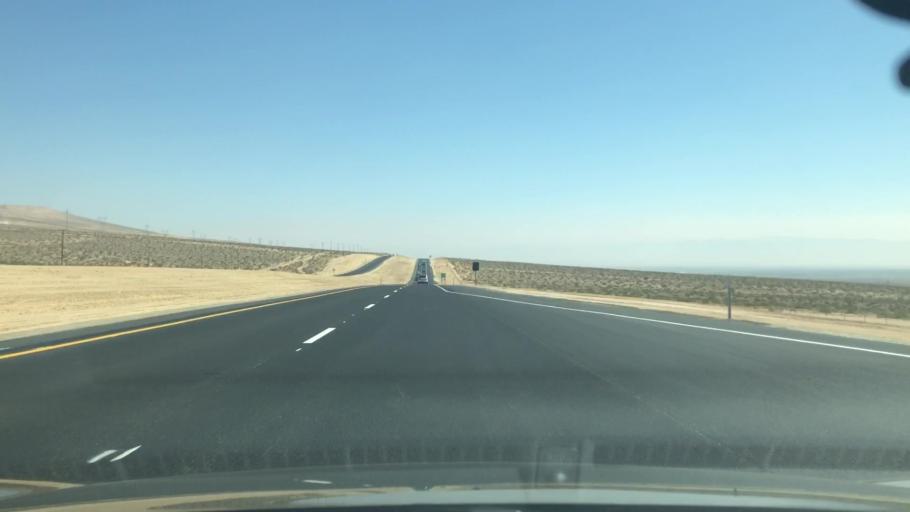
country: US
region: California
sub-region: Kern County
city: Inyokern
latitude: 35.6205
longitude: -117.8928
